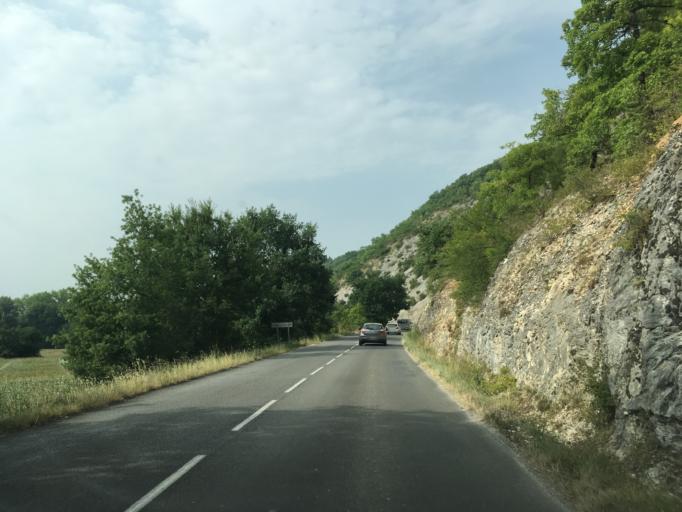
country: FR
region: Midi-Pyrenees
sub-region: Departement du Lot
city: Souillac
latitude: 44.8668
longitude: 1.4986
